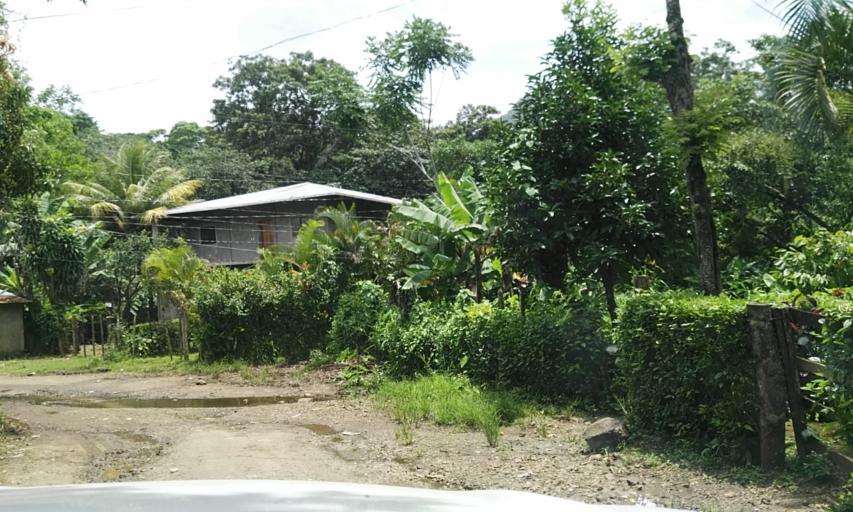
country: NI
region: Matagalpa
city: San Ramon
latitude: 12.9813
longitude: -85.8432
